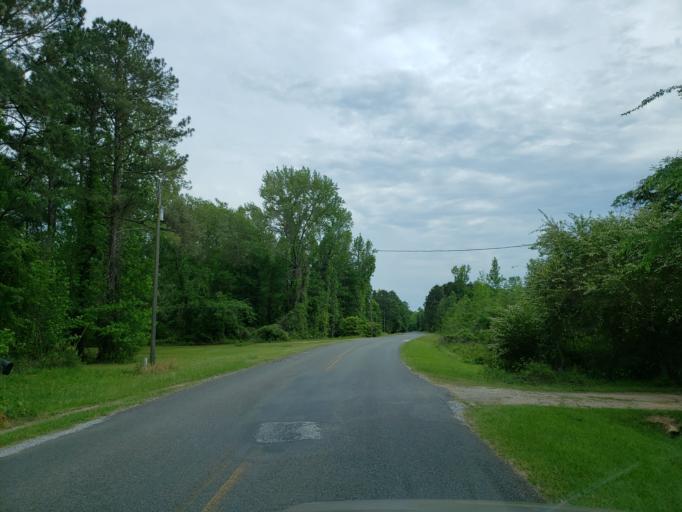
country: US
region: Georgia
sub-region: Bibb County
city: West Point
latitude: 32.8533
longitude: -83.8915
